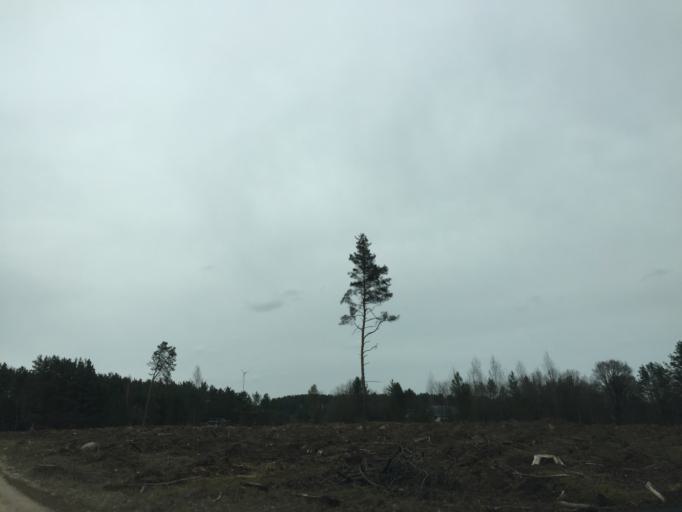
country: LV
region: Jekabpils Rajons
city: Jekabpils
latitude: 56.4858
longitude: 25.9003
